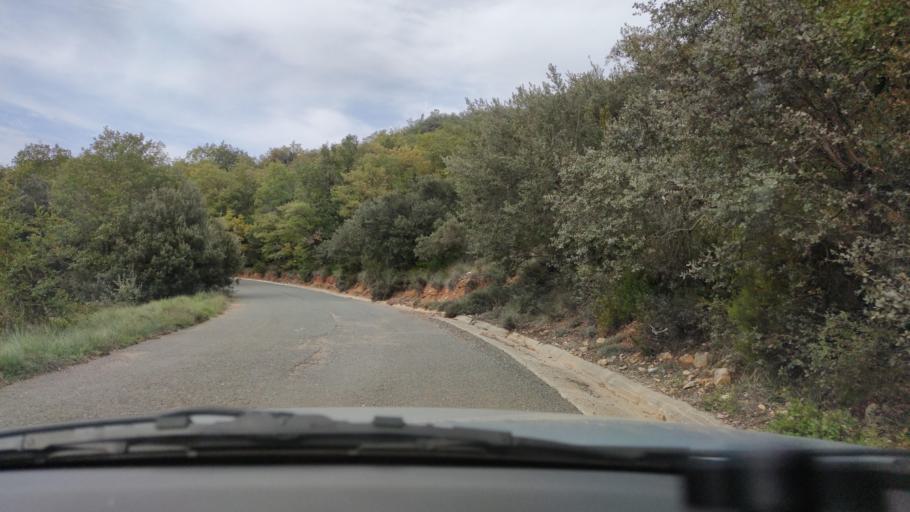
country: ES
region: Catalonia
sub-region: Provincia de Lleida
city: Llimiana
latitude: 42.0375
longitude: 1.0162
